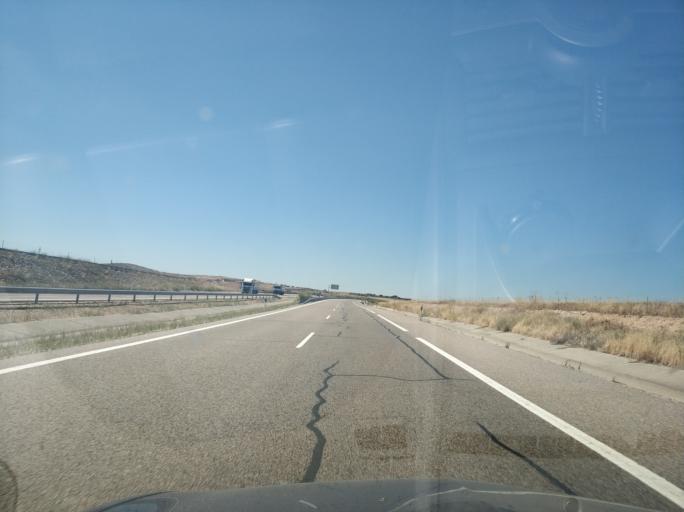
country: ES
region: Castille and Leon
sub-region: Provincia de Salamanca
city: Aldeatejada
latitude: 40.9248
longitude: -5.6714
